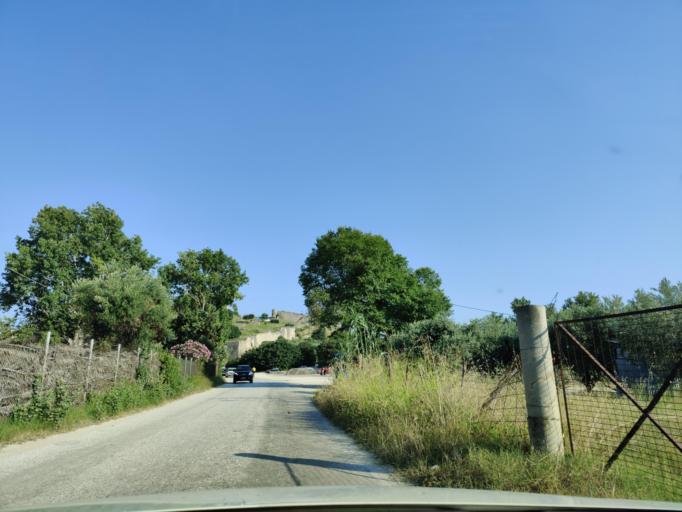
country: GR
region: East Macedonia and Thrace
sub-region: Nomos Kavalas
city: Nea Peramos
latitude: 40.8269
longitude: 24.3066
